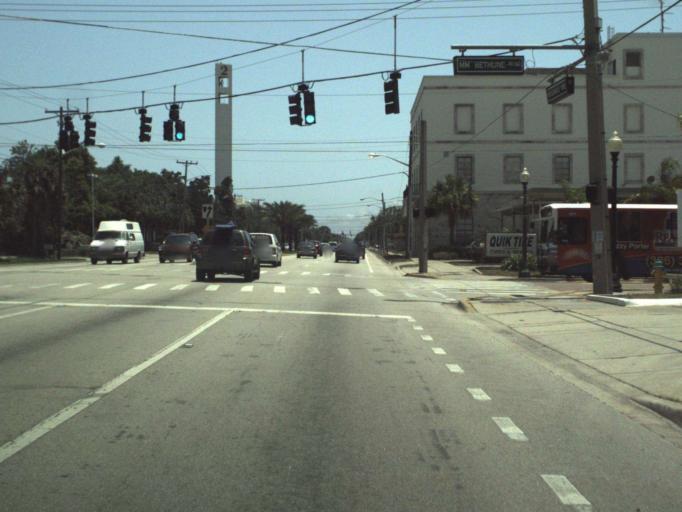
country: US
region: Florida
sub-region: Volusia County
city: Daytona Beach
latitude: 29.2158
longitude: -81.0255
